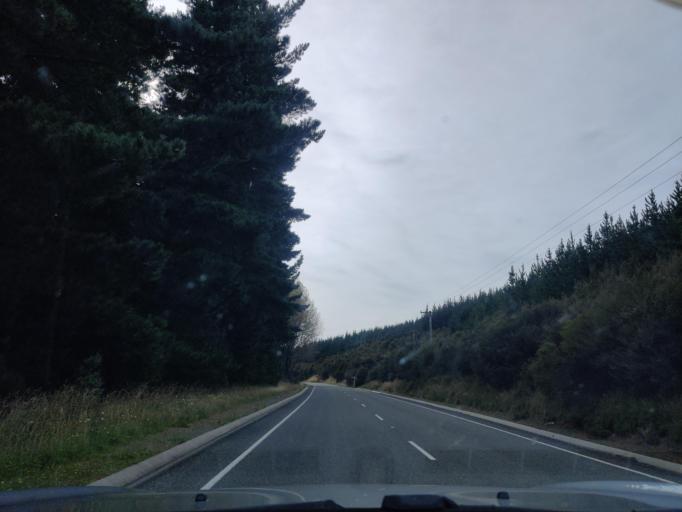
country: NZ
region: Tasman
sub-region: Tasman District
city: Brightwater
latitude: -41.6630
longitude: 173.2138
